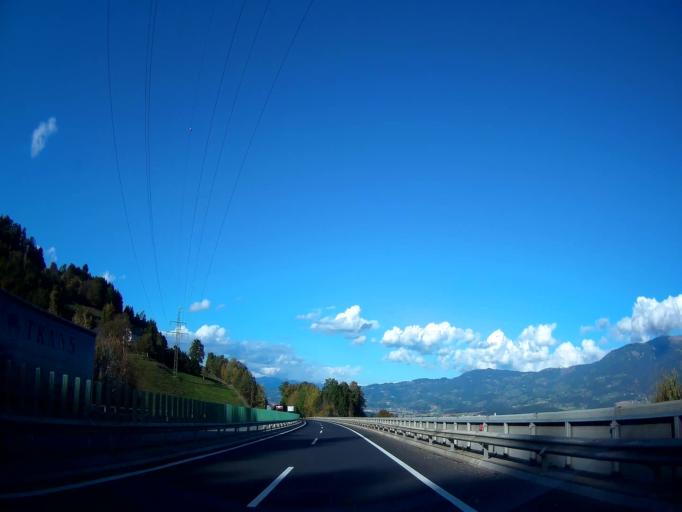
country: AT
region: Carinthia
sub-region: Politischer Bezirk Wolfsberg
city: Sankt Andrae
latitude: 46.7513
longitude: 14.8154
